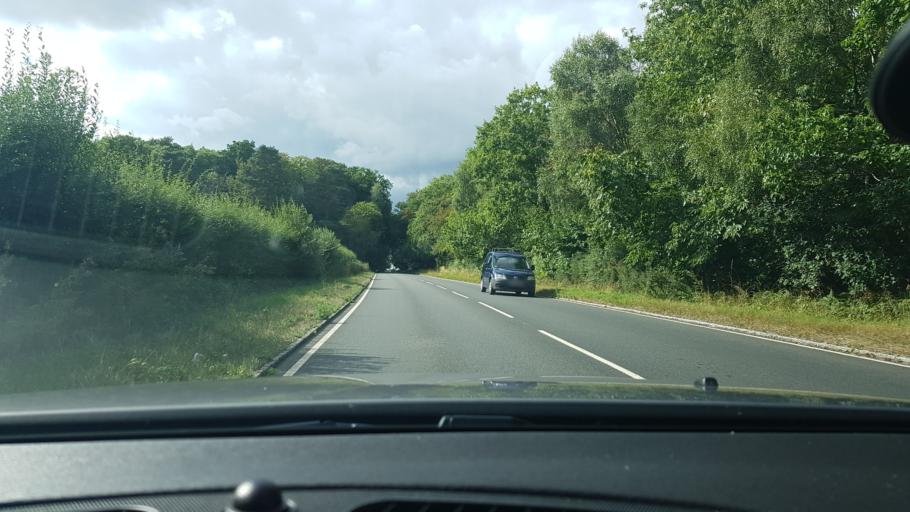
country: GB
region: England
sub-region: West Berkshire
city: Wickham
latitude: 51.4308
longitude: -1.4103
